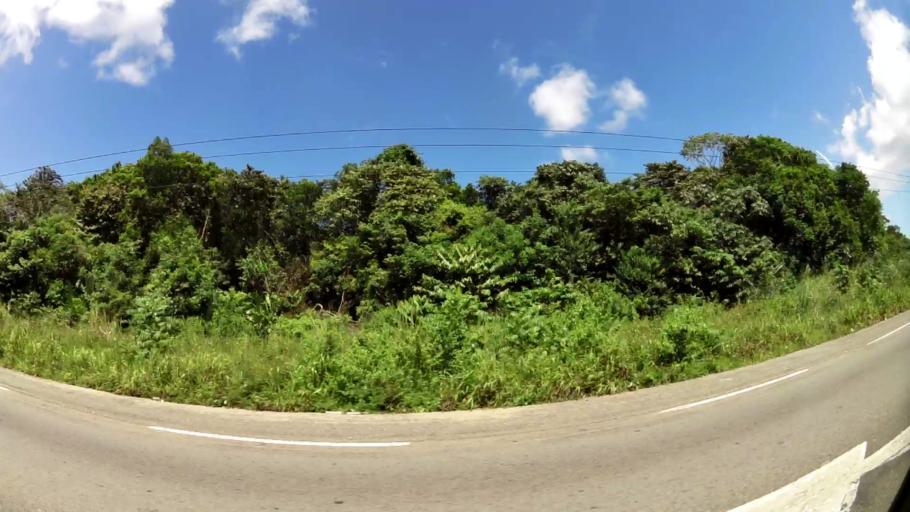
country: GF
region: Guyane
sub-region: Guyane
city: Matoury
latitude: 4.8698
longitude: -52.3364
